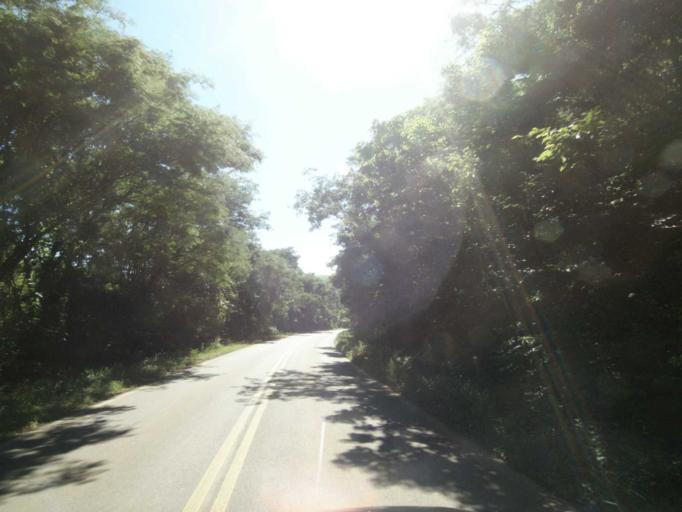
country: BR
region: Parana
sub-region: Francisco Beltrao
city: Francisco Beltrao
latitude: -26.1457
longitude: -53.3182
